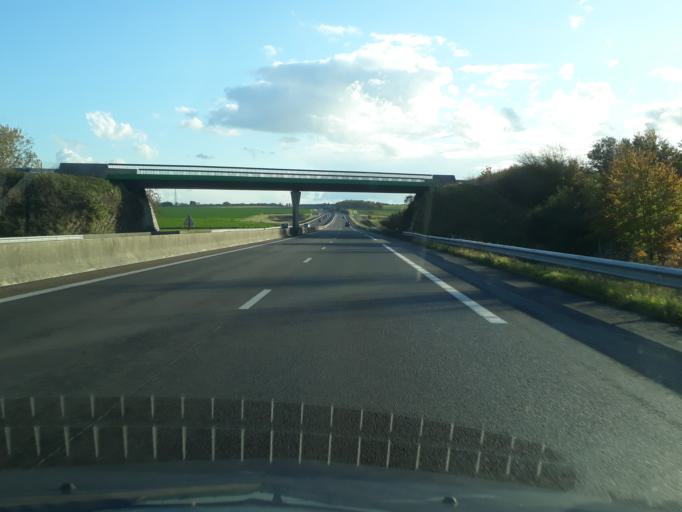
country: FR
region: Champagne-Ardenne
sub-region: Departement de la Marne
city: Fagnieres
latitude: 48.9231
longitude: 4.2832
